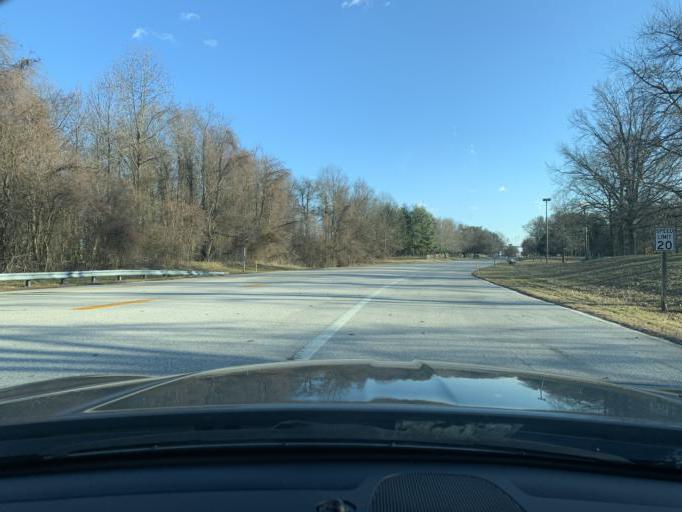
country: US
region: Maryland
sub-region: Anne Arundel County
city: Cape Saint Claire
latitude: 39.0186
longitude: -76.4031
